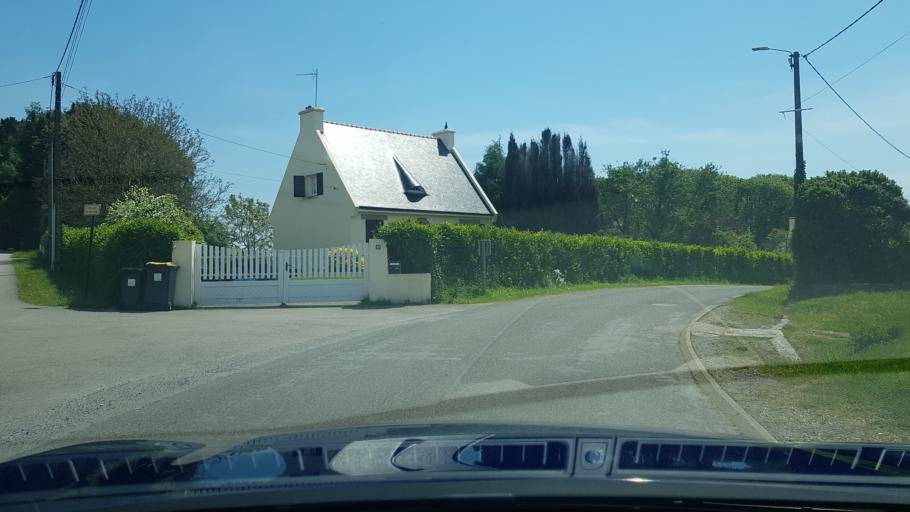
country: FR
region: Brittany
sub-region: Departement du Morbihan
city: Gestel
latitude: 47.8124
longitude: -3.4237
